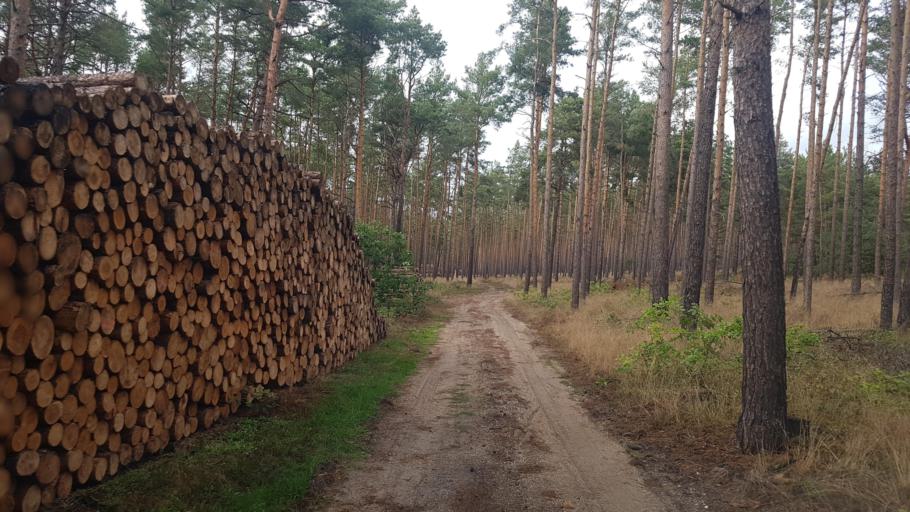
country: DE
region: Brandenburg
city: Elsterwerda
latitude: 51.4852
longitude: 13.4626
